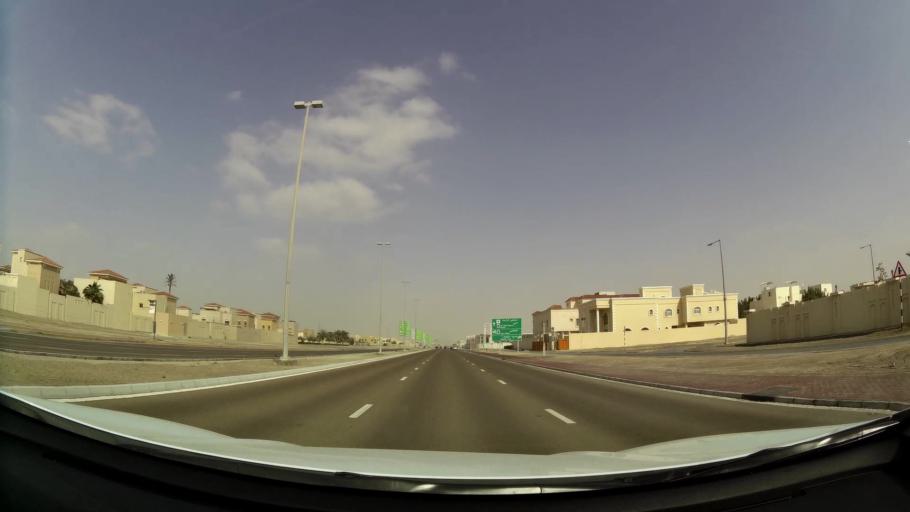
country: AE
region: Abu Dhabi
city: Abu Dhabi
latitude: 24.4284
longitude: 54.5593
